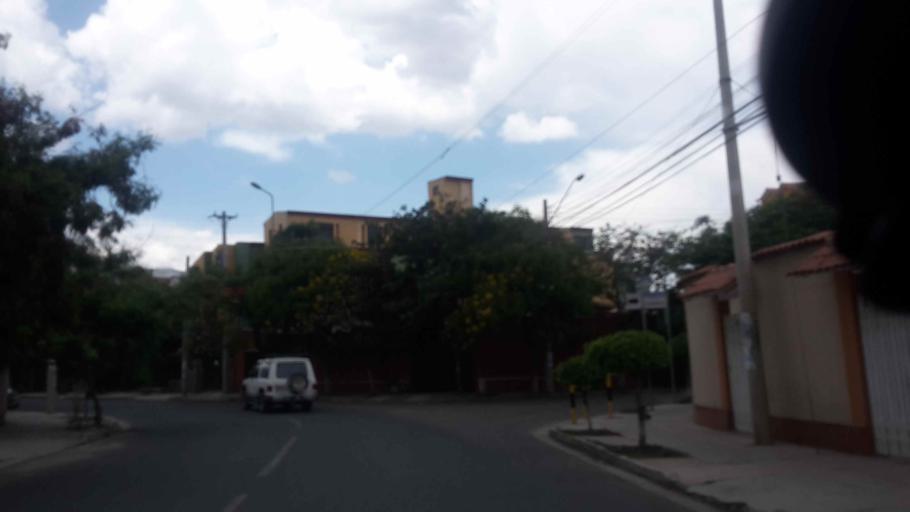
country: BO
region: Cochabamba
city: Cochabamba
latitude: -17.4011
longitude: -66.1734
